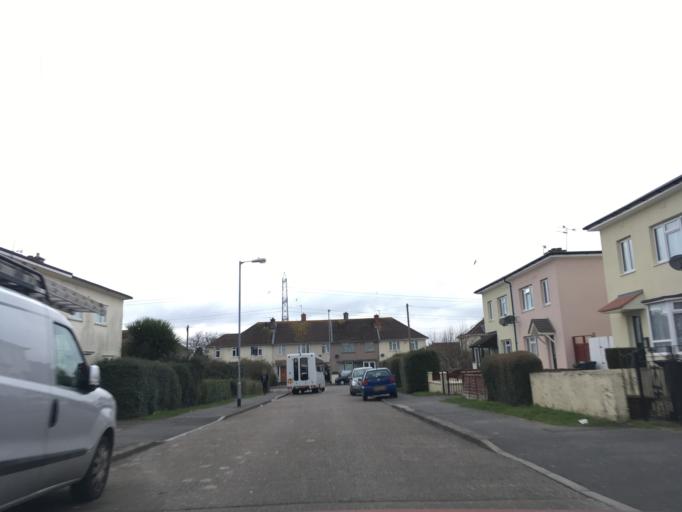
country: GB
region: England
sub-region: South Gloucestershire
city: Stoke Gifford
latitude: 51.4952
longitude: -2.5645
